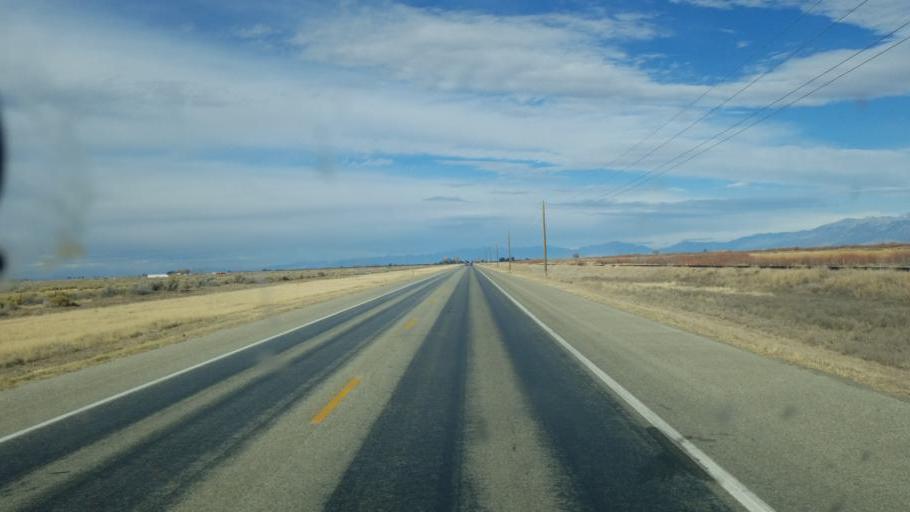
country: US
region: Colorado
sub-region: Alamosa County
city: Alamosa
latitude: 37.3213
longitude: -105.9481
